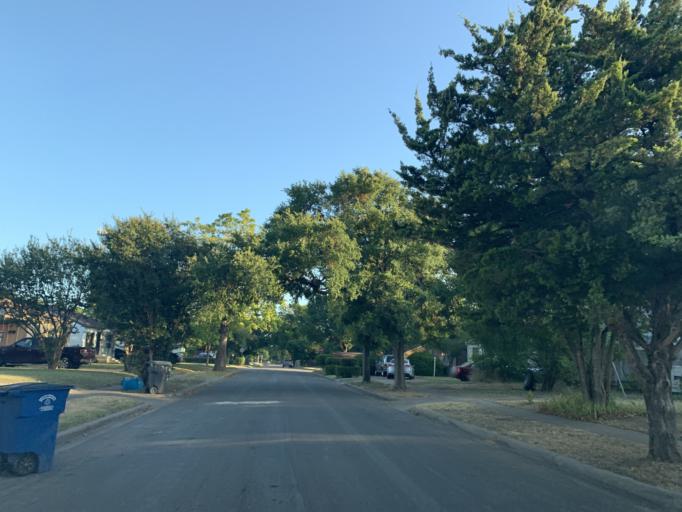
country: US
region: Texas
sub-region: Dallas County
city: Dallas
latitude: 32.7037
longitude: -96.8095
